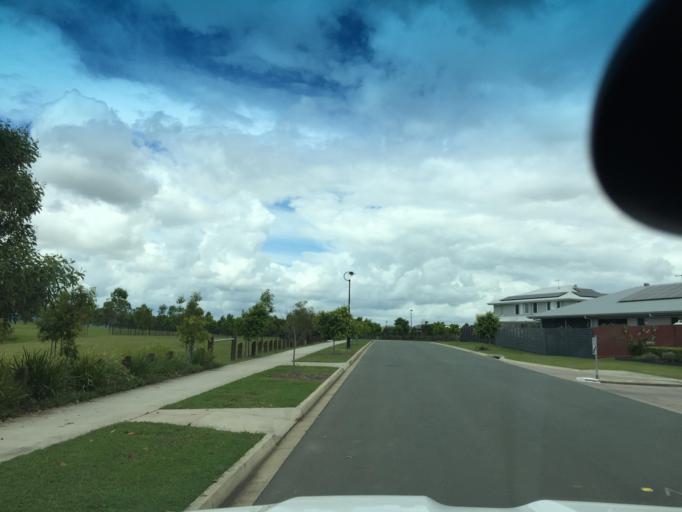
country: AU
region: Queensland
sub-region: Moreton Bay
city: Caboolture South
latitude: -27.0942
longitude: 152.9664
